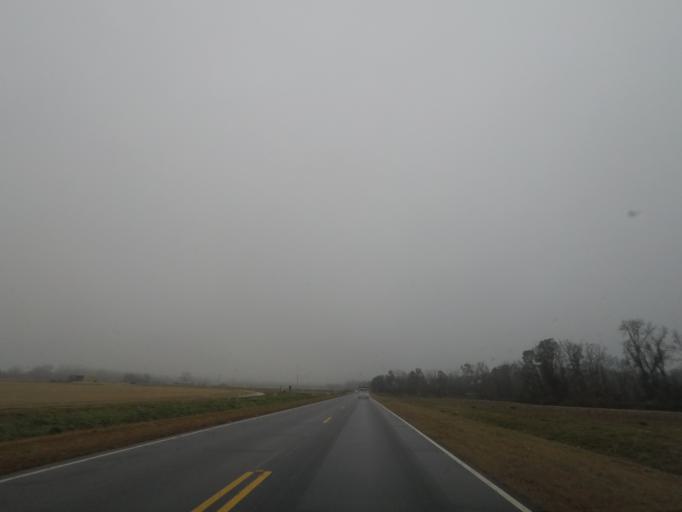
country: US
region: North Carolina
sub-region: Scotland County
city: Laurinburg
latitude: 34.7772
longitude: -79.4312
